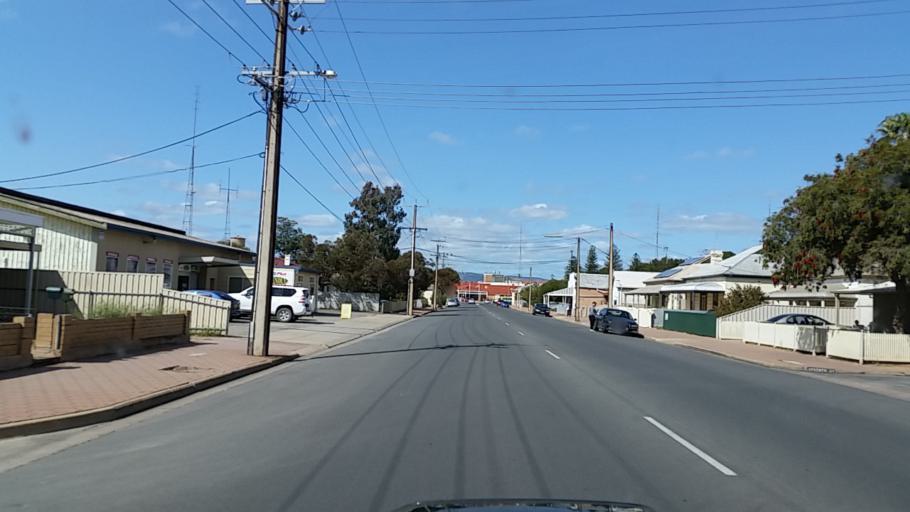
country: AU
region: South Australia
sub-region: Port Pirie City and Dists
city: Port Pirie
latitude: -33.1772
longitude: 138.0014
